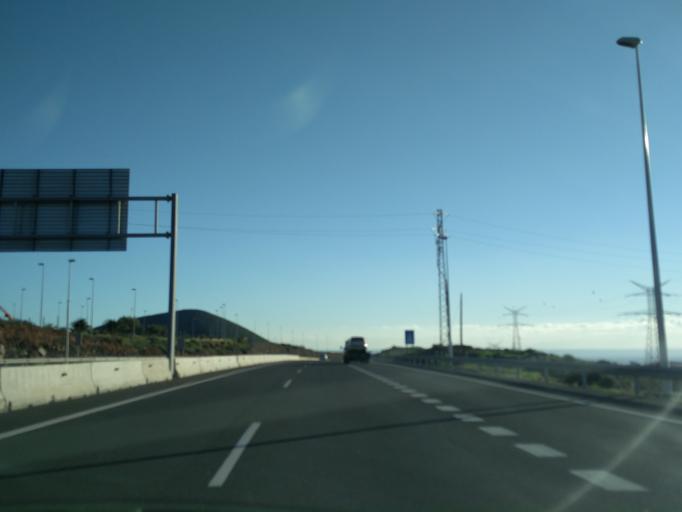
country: ES
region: Canary Islands
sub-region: Provincia de Santa Cruz de Tenerife
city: San Isidro
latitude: 28.0714
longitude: -16.5527
